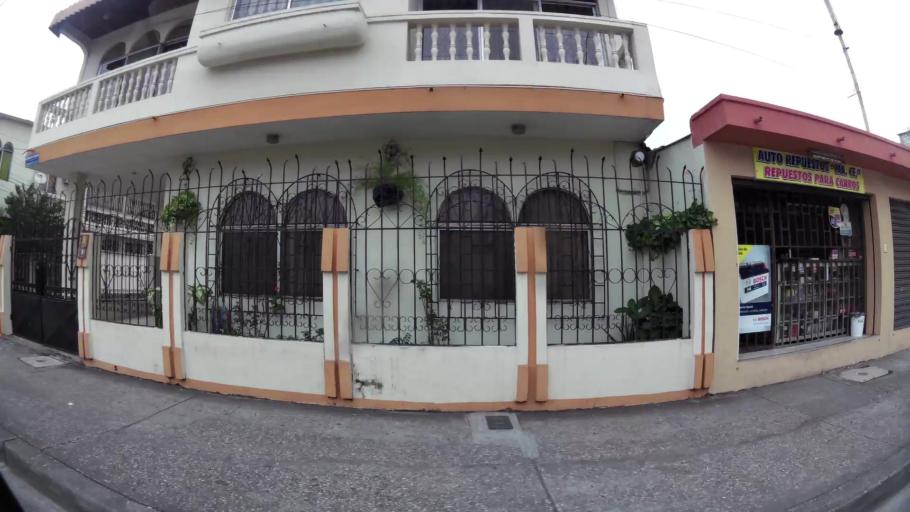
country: EC
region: Guayas
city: Eloy Alfaro
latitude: -2.1399
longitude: -79.8940
